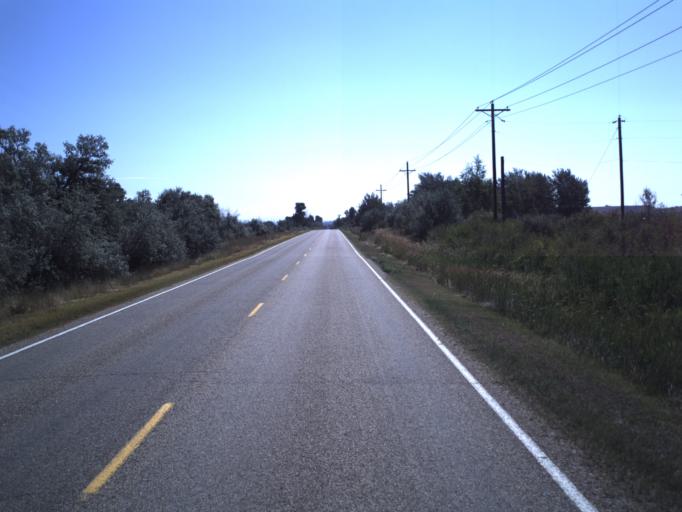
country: US
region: Utah
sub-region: Duchesne County
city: Roosevelt
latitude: 40.2581
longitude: -110.1322
